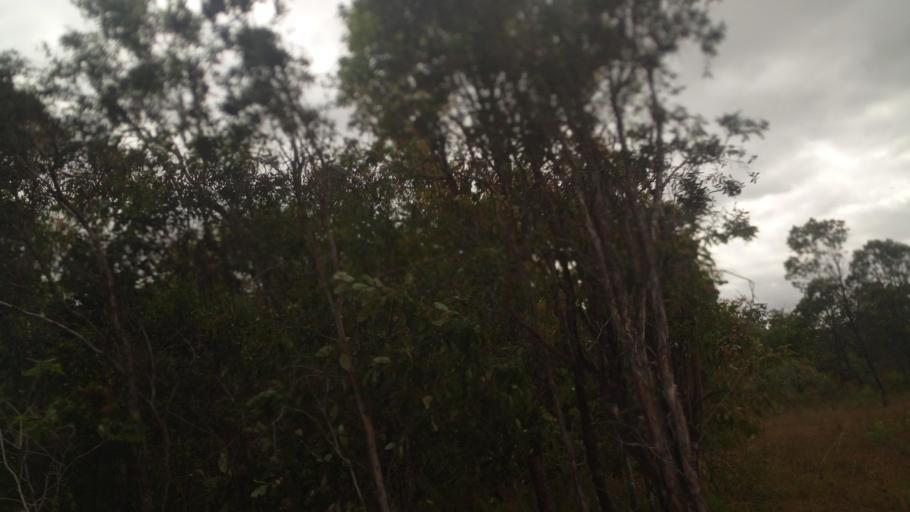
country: AU
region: Queensland
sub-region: Tablelands
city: Mareeba
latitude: -16.9630
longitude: 145.4421
